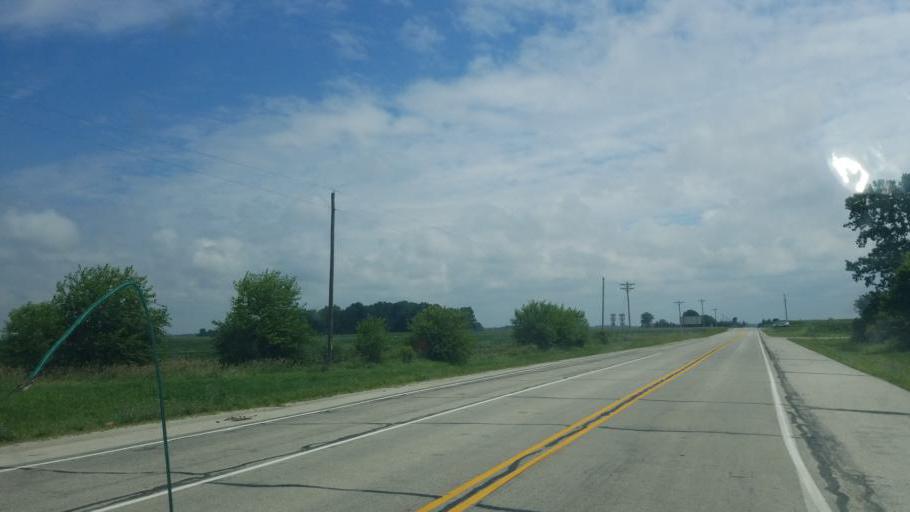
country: US
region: Indiana
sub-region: Huntington County
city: Warren
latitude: 40.6679
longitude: -85.4920
